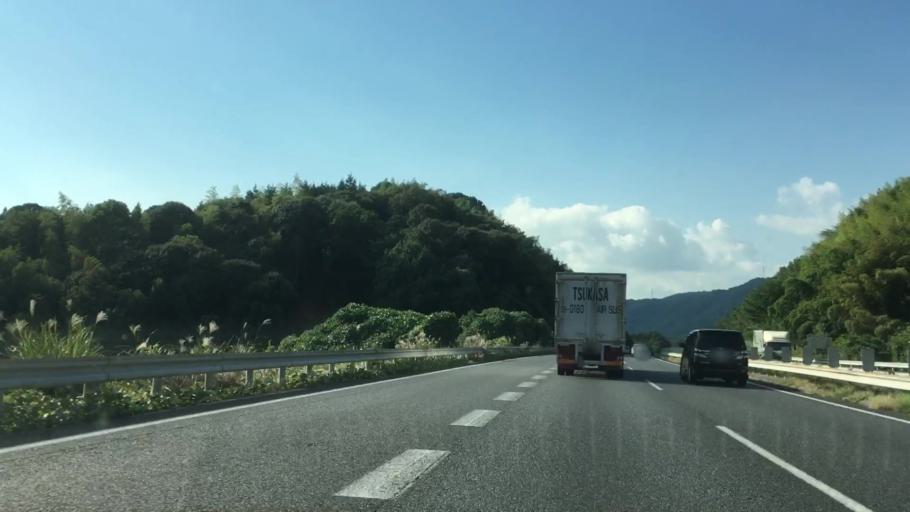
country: JP
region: Yamaguchi
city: Kudamatsu
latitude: 34.0333
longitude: 131.9314
